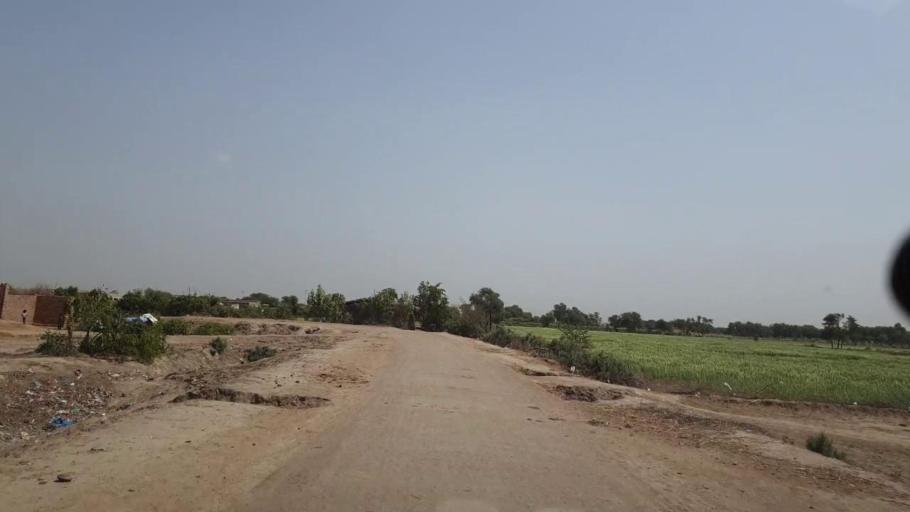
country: PK
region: Sindh
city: Matli
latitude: 25.0799
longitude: 68.6906
